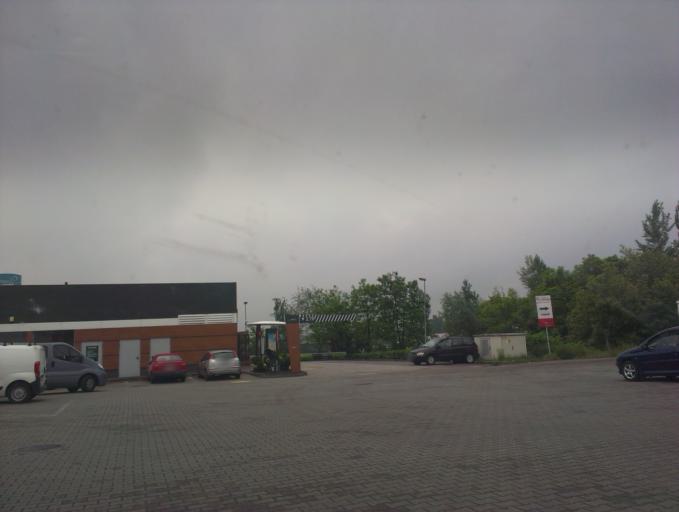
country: PL
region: Silesian Voivodeship
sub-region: Katowice
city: Katowice
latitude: 50.2450
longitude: 19.0303
